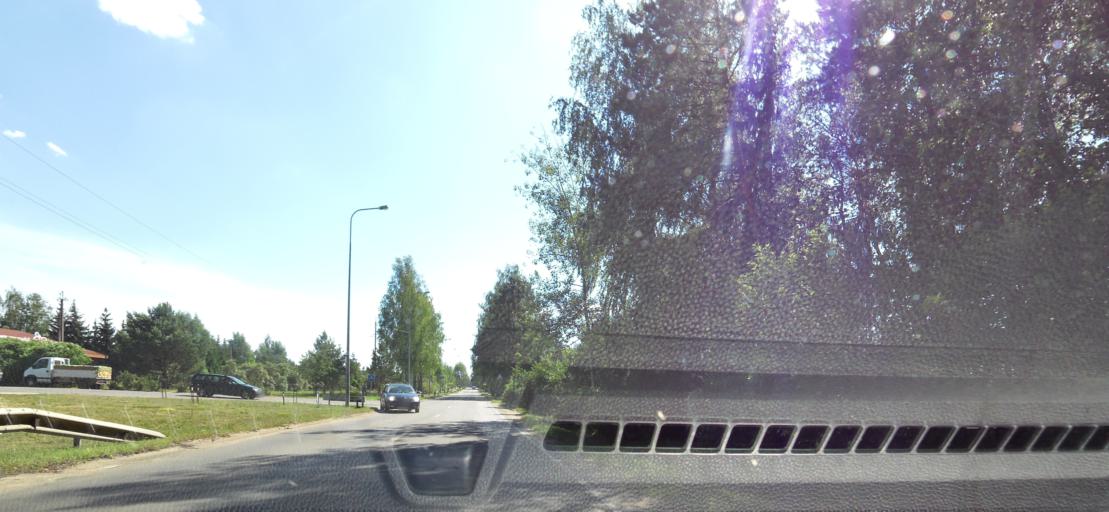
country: LT
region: Vilnius County
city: Rasos
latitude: 54.7863
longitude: 25.3476
